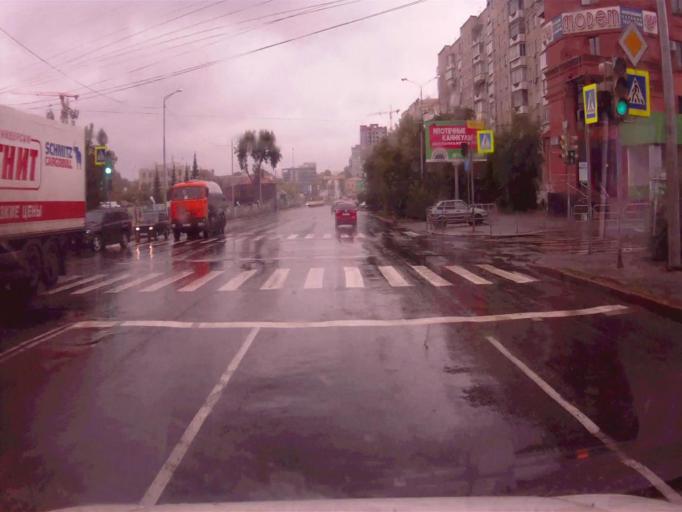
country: RU
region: Chelyabinsk
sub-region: Gorod Chelyabinsk
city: Chelyabinsk
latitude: 55.1638
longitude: 61.4162
